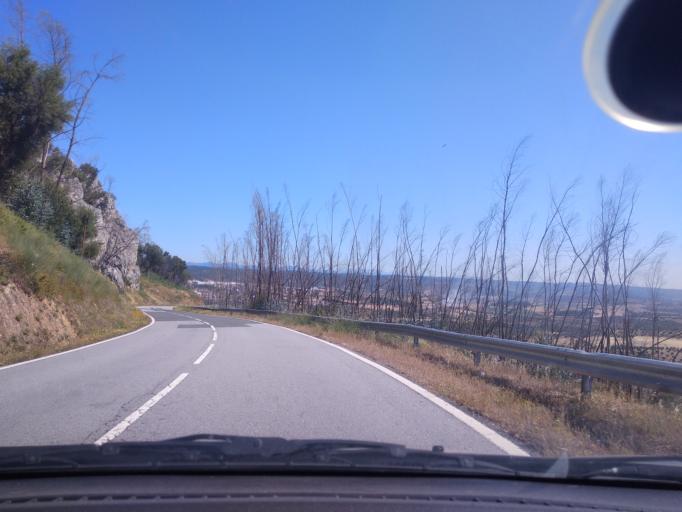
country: PT
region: Portalegre
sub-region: Nisa
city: Nisa
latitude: 39.6291
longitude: -7.6630
